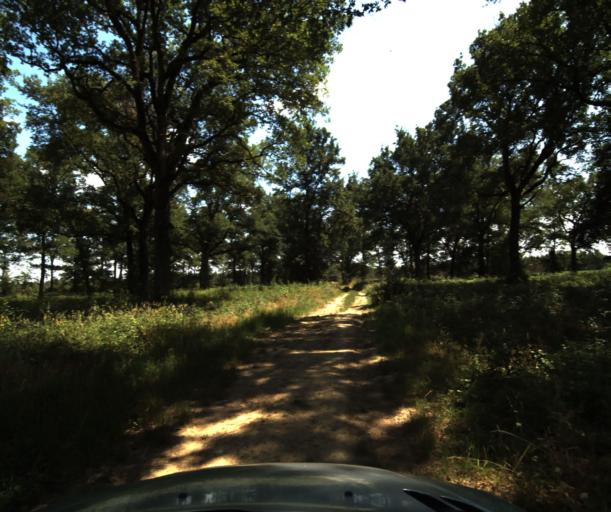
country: FR
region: Midi-Pyrenees
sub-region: Departement de la Haute-Garonne
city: Labastidette
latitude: 43.4611
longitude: 1.2287
